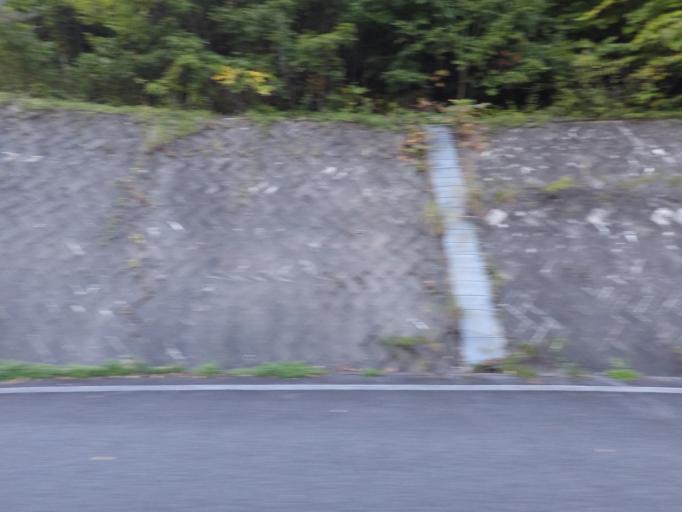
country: JP
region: Nagano
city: Tatsuno
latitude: 35.9821
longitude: 137.7672
